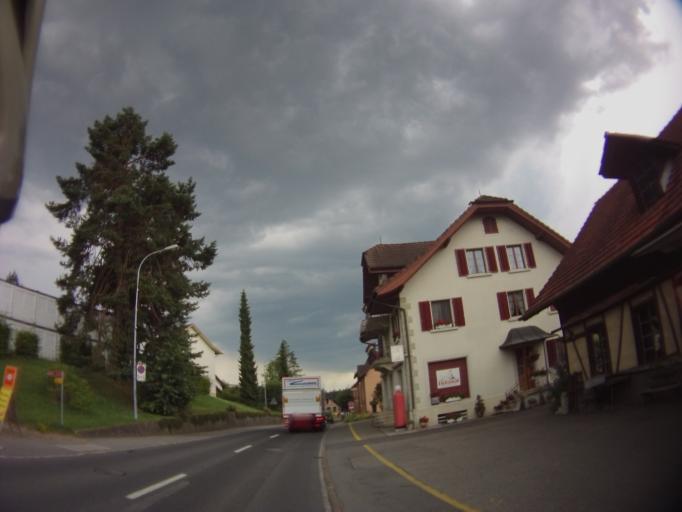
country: CH
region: Zug
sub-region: Zug
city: Hunenberg
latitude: 47.1740
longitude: 8.4268
